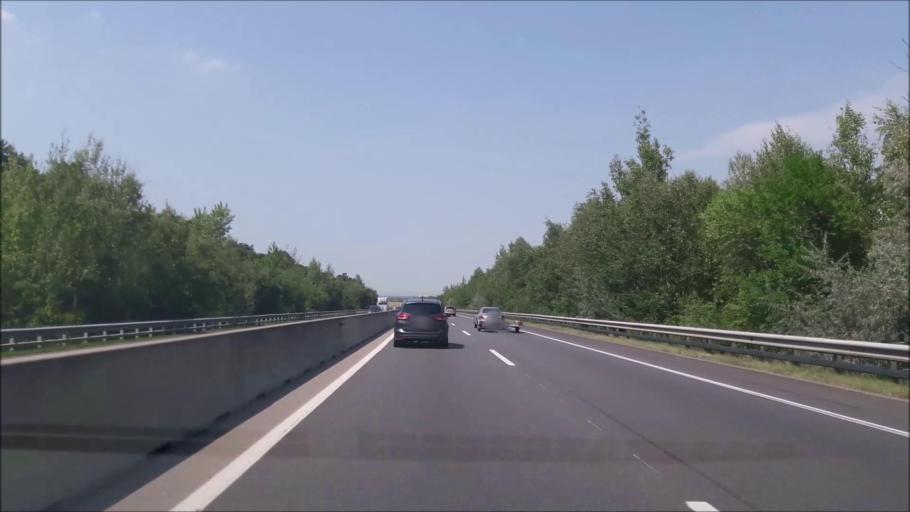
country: AT
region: Lower Austria
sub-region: Politischer Bezirk Ganserndorf
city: Mannsdorf an der Donau
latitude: 48.0888
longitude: 16.6686
